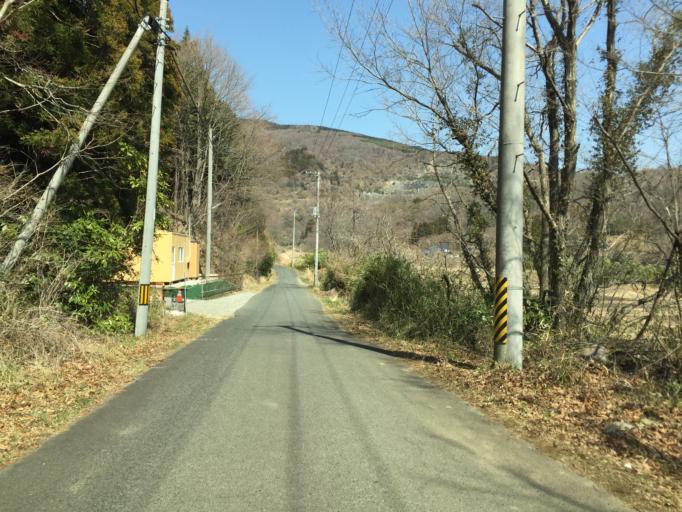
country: JP
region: Fukushima
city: Iwaki
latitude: 37.0037
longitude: 140.7940
